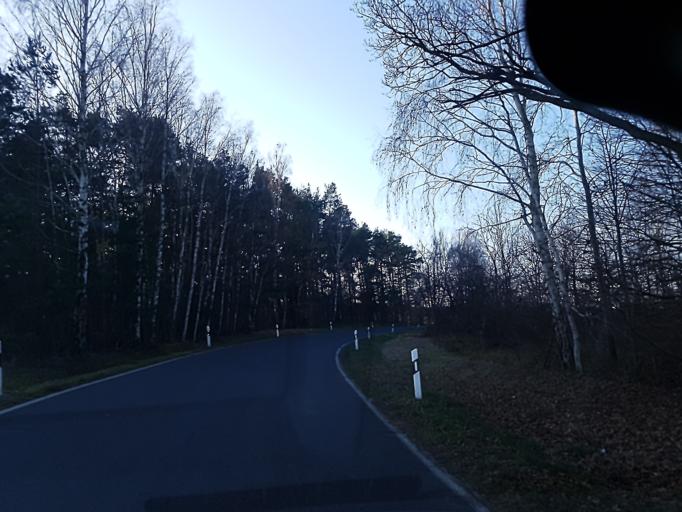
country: DE
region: Brandenburg
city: Schonborn
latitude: 51.5529
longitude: 13.4917
